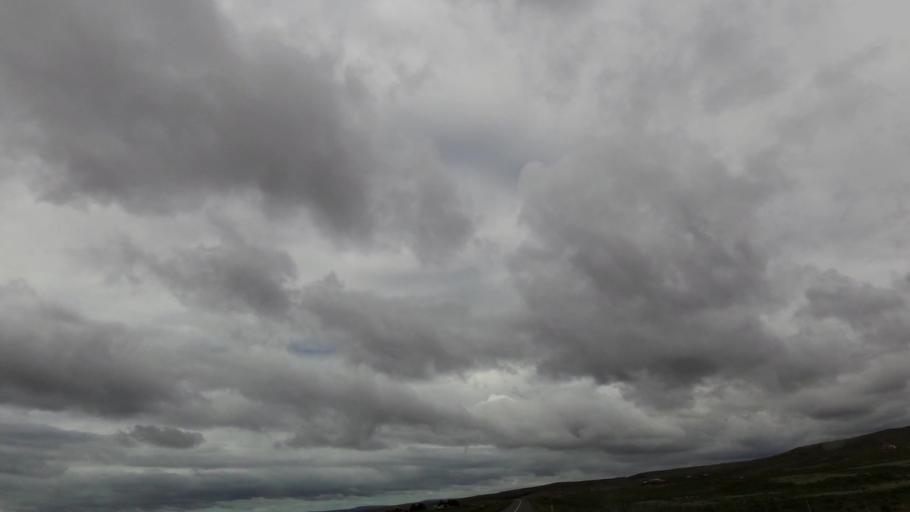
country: IS
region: West
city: Borgarnes
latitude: 65.0100
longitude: -21.6383
